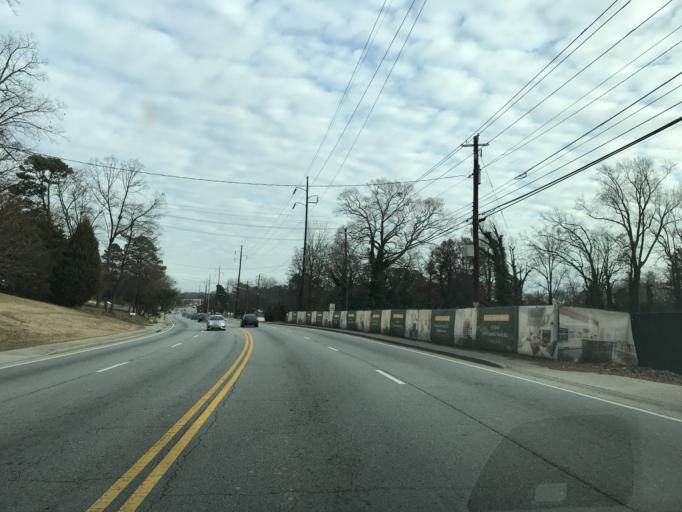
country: US
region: Georgia
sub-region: DeKalb County
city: Doraville
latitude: 33.8833
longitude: -84.2818
